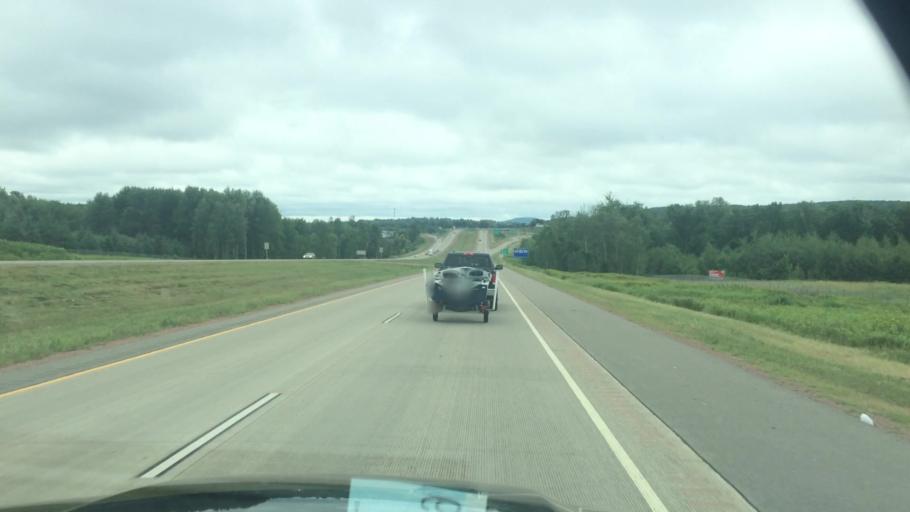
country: US
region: Wisconsin
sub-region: Marathon County
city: Wausau
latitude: 45.0015
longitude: -89.6585
